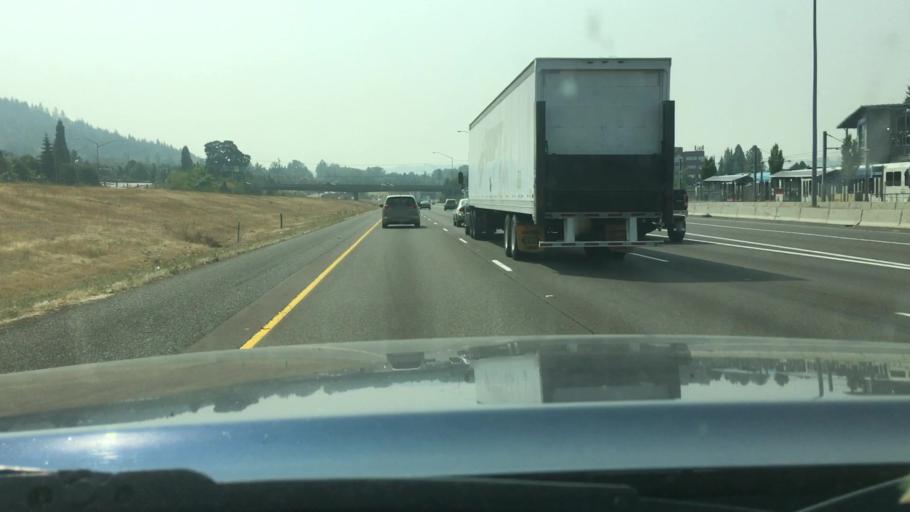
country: US
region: Oregon
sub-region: Clackamas County
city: Clackamas
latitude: 45.4366
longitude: -122.5676
